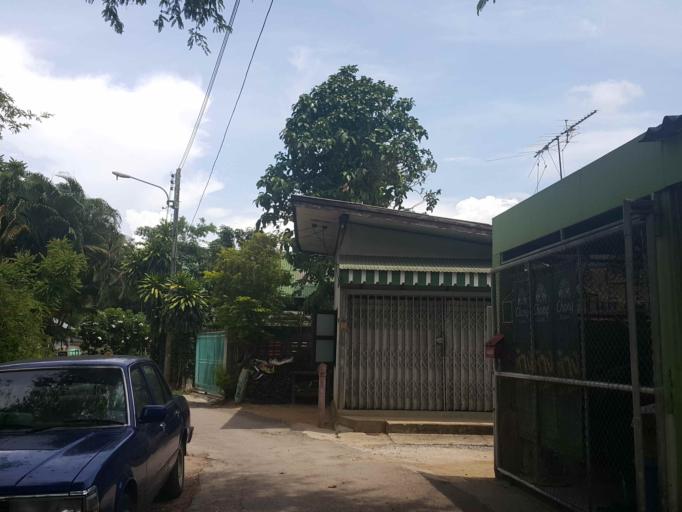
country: TH
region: Chiang Mai
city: Chiang Mai
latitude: 18.7625
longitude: 99.0126
